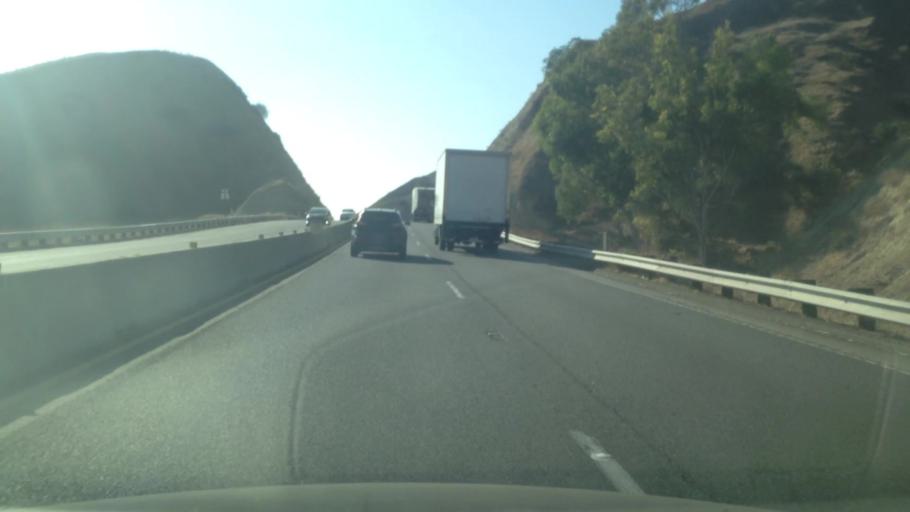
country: US
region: California
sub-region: Riverside County
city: Calimesa
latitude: 33.9426
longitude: -117.0873
